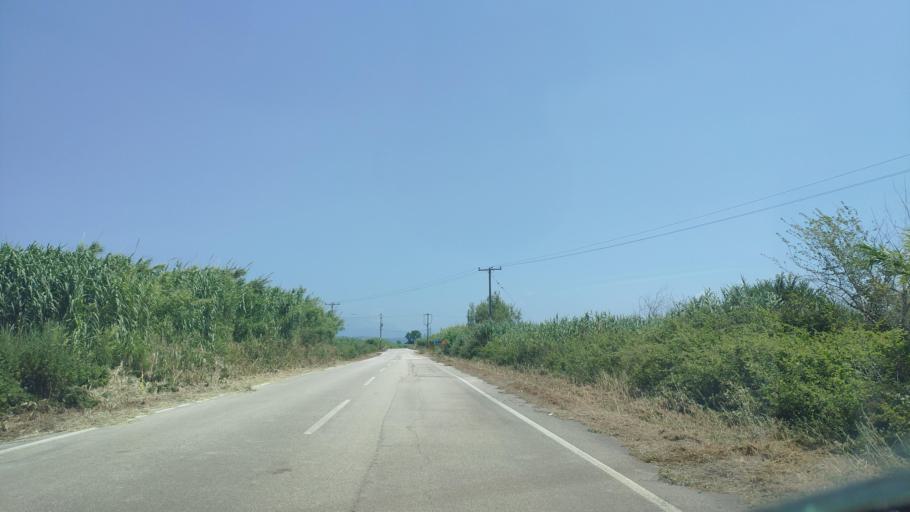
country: GR
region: Epirus
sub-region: Nomos Artas
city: Aneza
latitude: 39.0769
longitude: 20.8843
